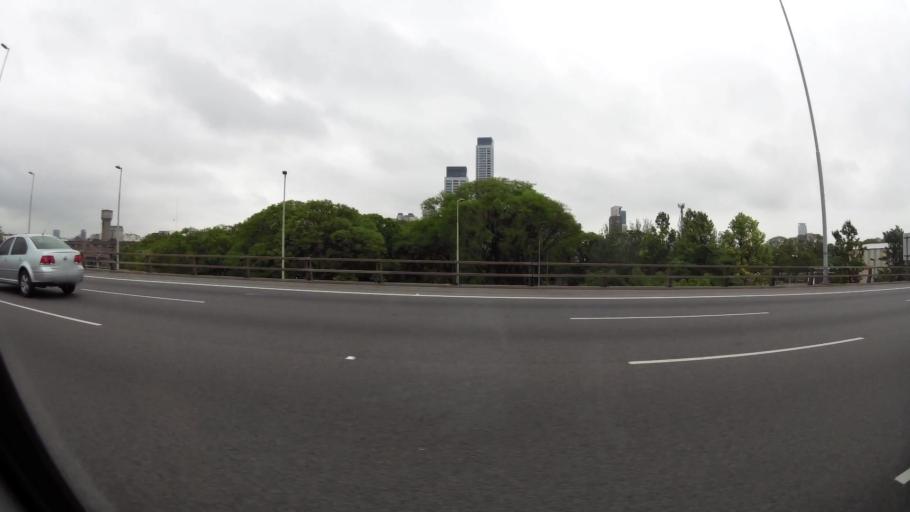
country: AR
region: Buenos Aires F.D.
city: Retiro
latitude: -34.5709
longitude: -58.4019
